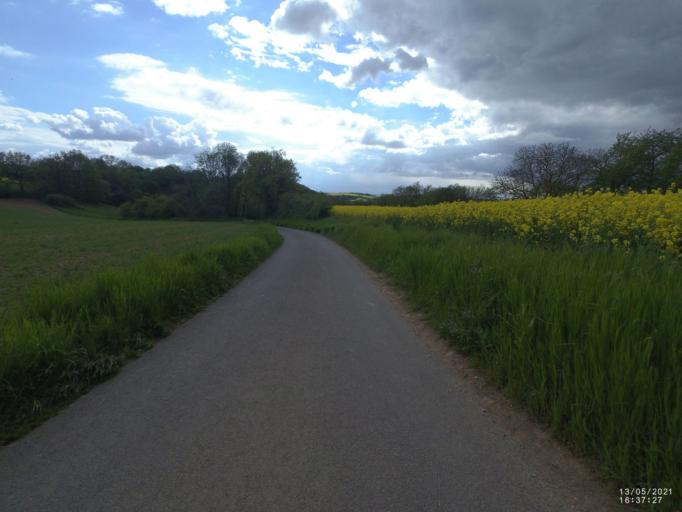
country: DE
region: Rheinland-Pfalz
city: Dieblich
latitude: 50.3236
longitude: 7.4605
